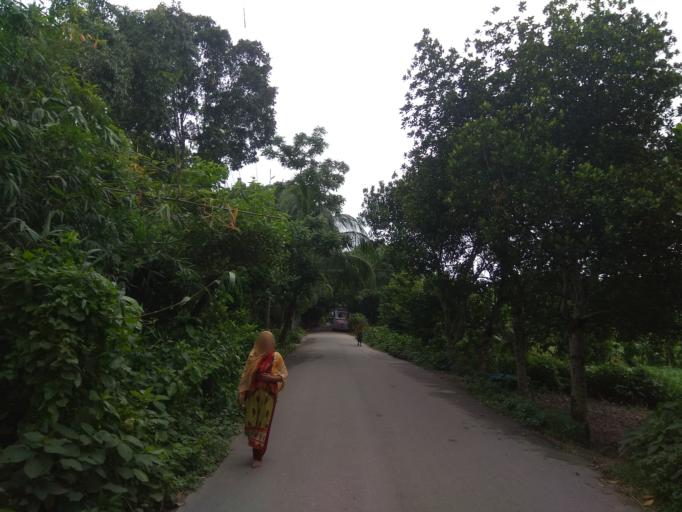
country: BD
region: Dhaka
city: Dohar
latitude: 23.4477
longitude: 90.0619
